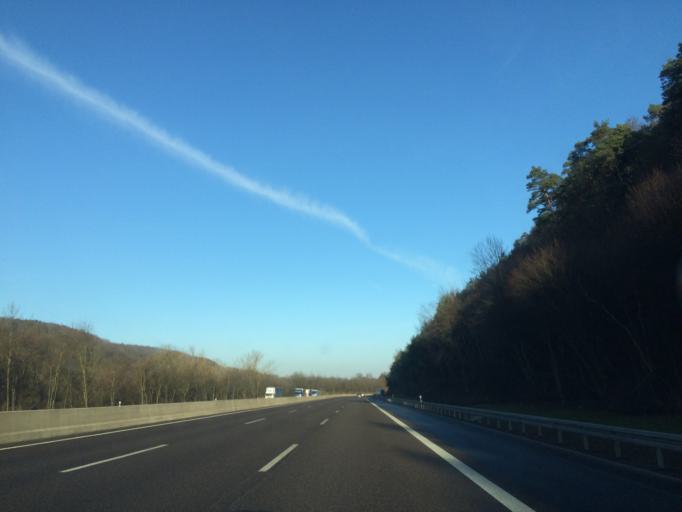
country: DE
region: Hesse
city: Schwarzenborn
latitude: 50.9775
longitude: 9.4727
